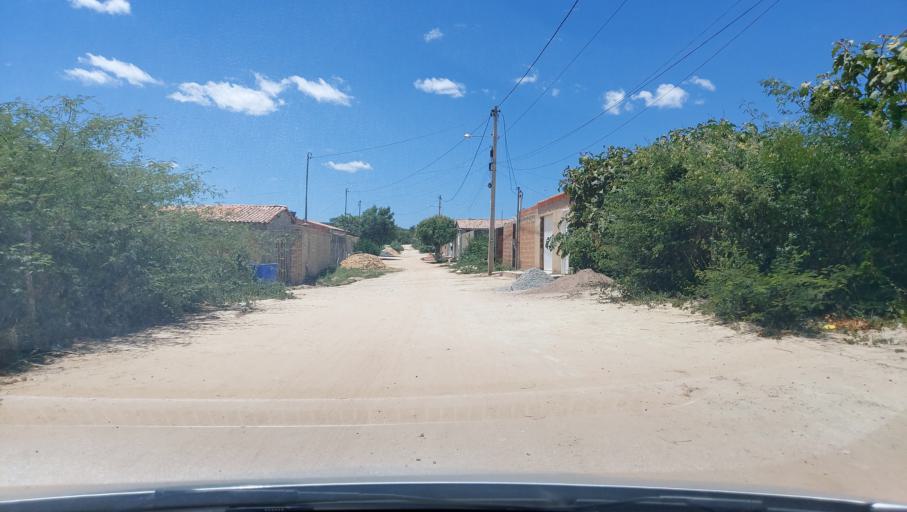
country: BR
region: Bahia
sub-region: Oliveira Dos Brejinhos
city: Beira Rio
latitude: -12.0069
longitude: -42.6301
